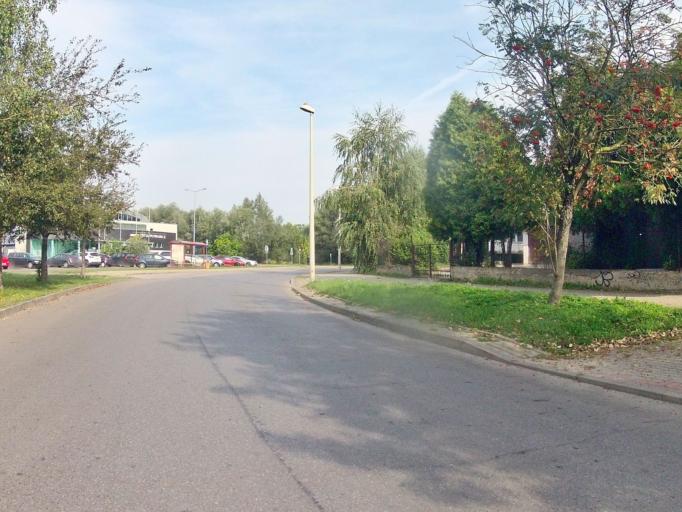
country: PL
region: Subcarpathian Voivodeship
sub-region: Powiat jasielski
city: Jaslo
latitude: 49.7442
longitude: 21.4575
